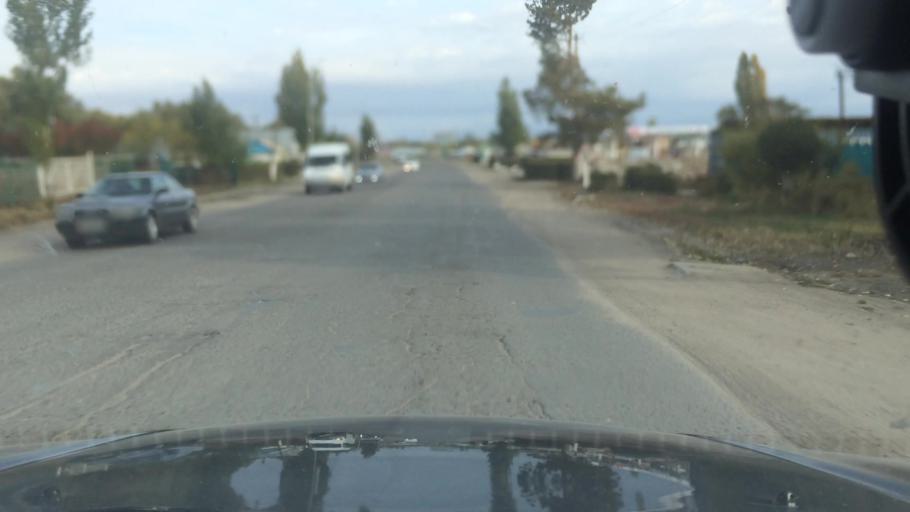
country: KG
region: Ysyk-Koel
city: Karakol
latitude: 42.5211
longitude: 78.3860
